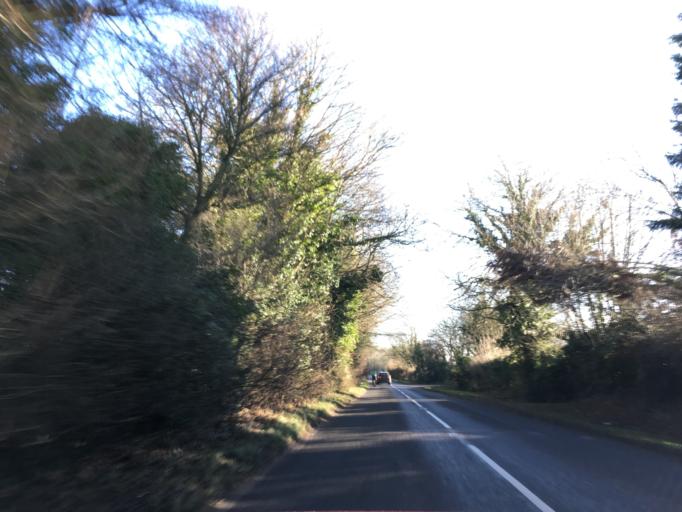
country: GB
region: England
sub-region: Wiltshire
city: Biddestone
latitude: 51.4944
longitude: -2.2151
